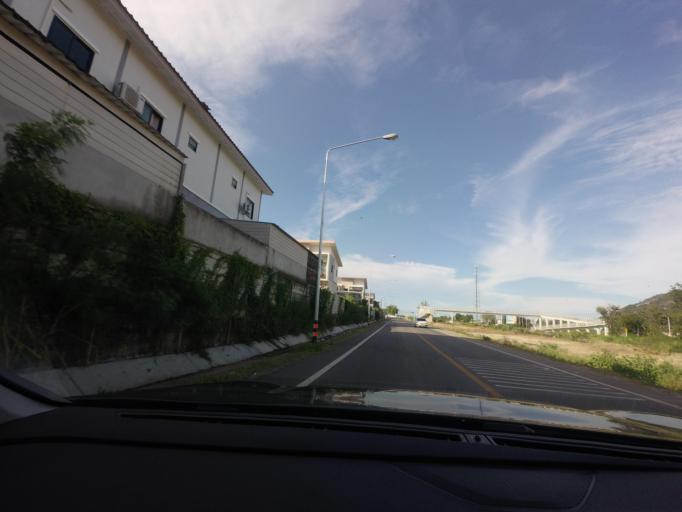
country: TH
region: Prachuap Khiri Khan
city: Pran Buri
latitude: 12.4458
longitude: 99.9619
